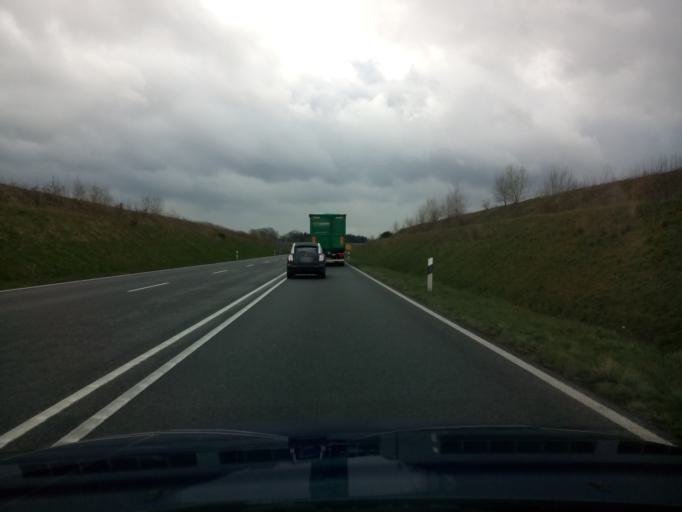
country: DE
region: Lower Saxony
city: Lastrup
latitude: 52.7912
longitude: 7.8396
